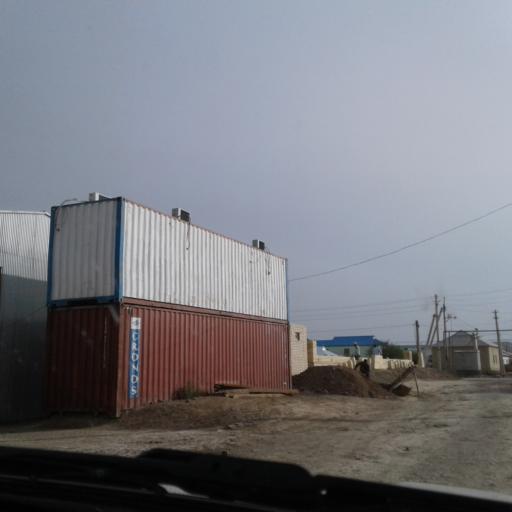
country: TM
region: Mary
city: Mary
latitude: 37.5802
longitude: 61.8731
